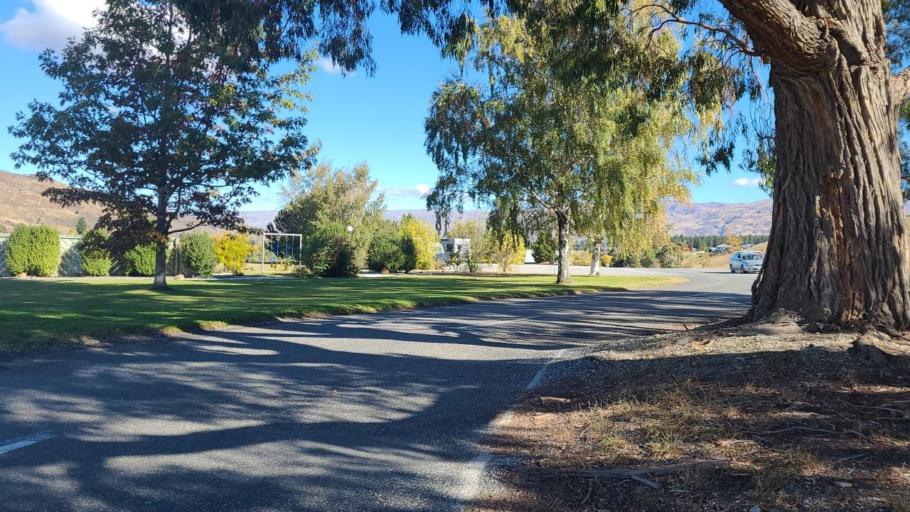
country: NZ
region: Otago
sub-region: Queenstown-Lakes District
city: Wanaka
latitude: -45.0489
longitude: 169.2022
